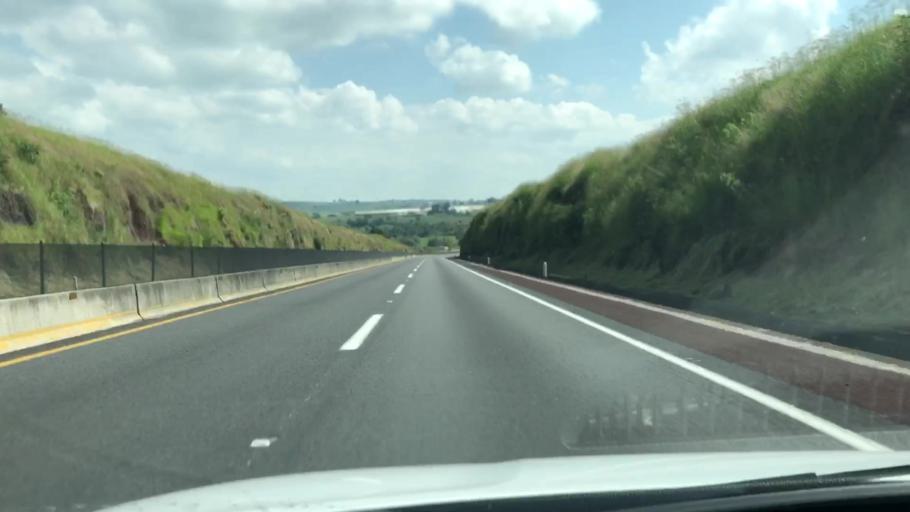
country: MX
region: Jalisco
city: Zapotlanejo
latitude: 20.6937
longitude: -102.9979
